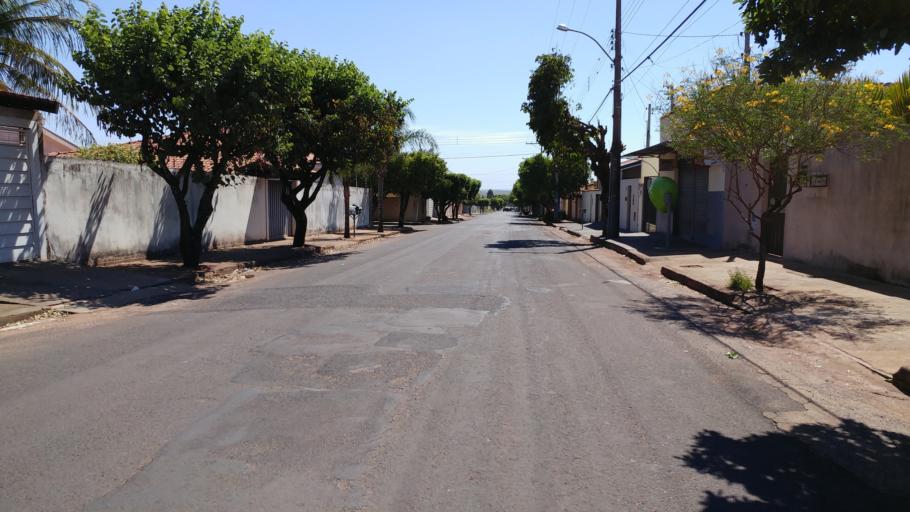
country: BR
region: Sao Paulo
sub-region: Paraguacu Paulista
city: Paraguacu Paulista
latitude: -22.4131
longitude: -50.5880
